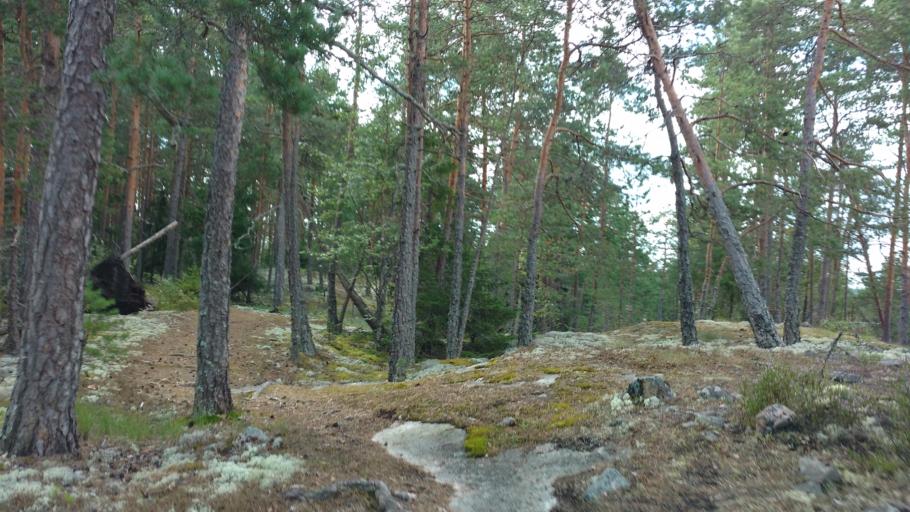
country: FI
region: Varsinais-Suomi
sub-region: Salo
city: Salo
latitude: 60.3670
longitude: 23.1789
